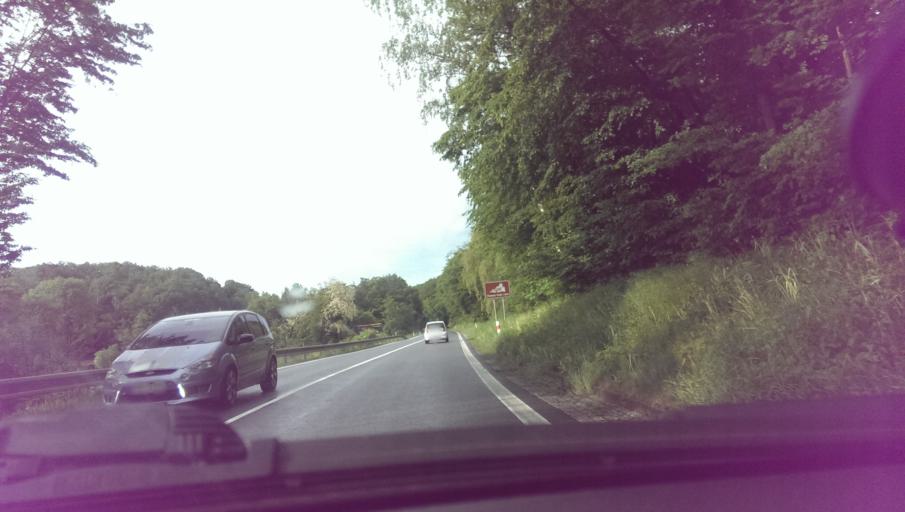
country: CZ
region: Zlin
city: Breznice
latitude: 49.1946
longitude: 17.6573
